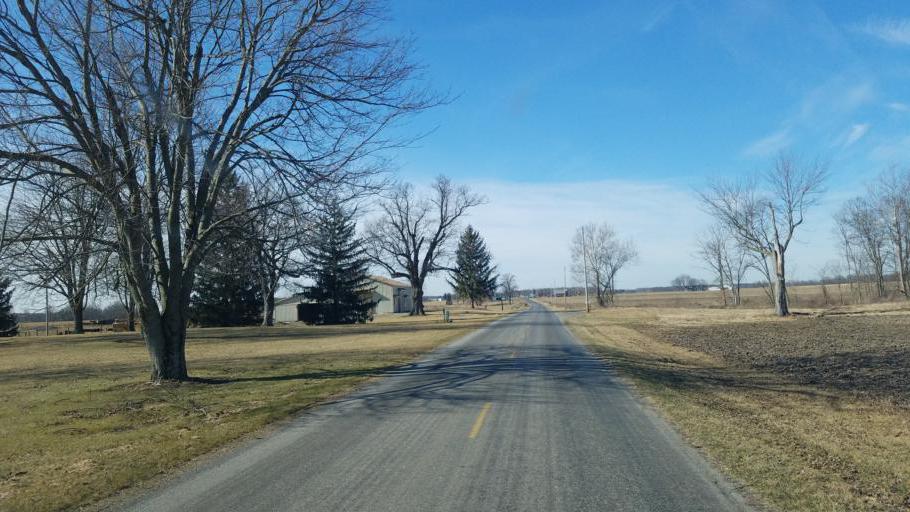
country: US
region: Ohio
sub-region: Hardin County
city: Kenton
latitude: 40.5920
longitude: -83.4394
